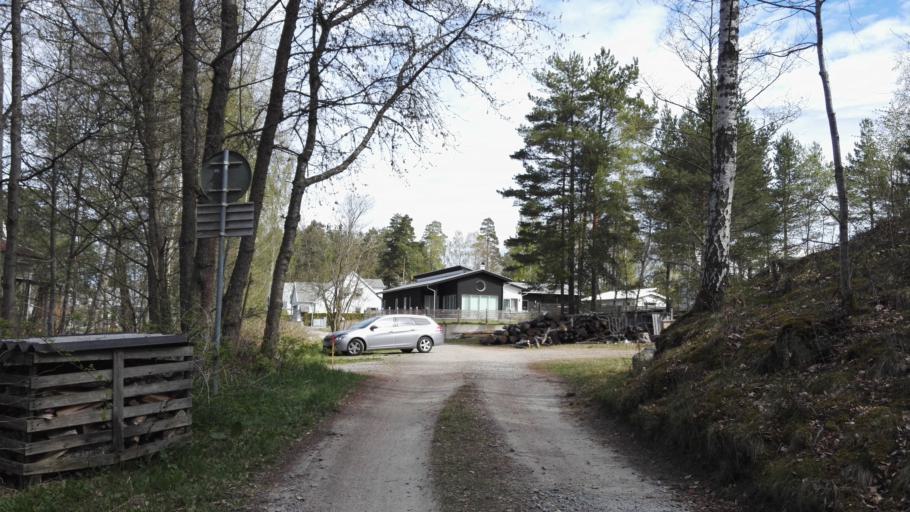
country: SE
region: Kronoberg
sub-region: Vaxjo Kommun
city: Vaexjoe
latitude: 56.9104
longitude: 14.7492
